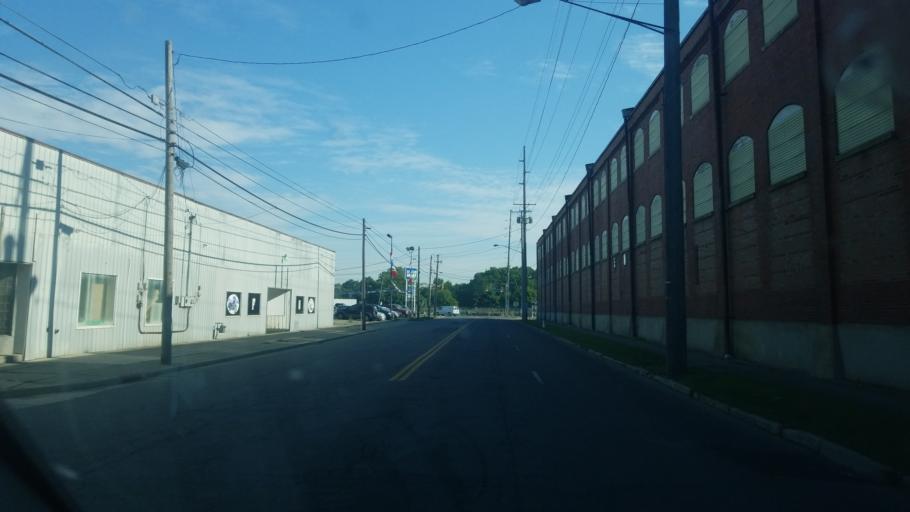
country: US
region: Ohio
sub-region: Marion County
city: Marion
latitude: 40.5873
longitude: -83.1433
